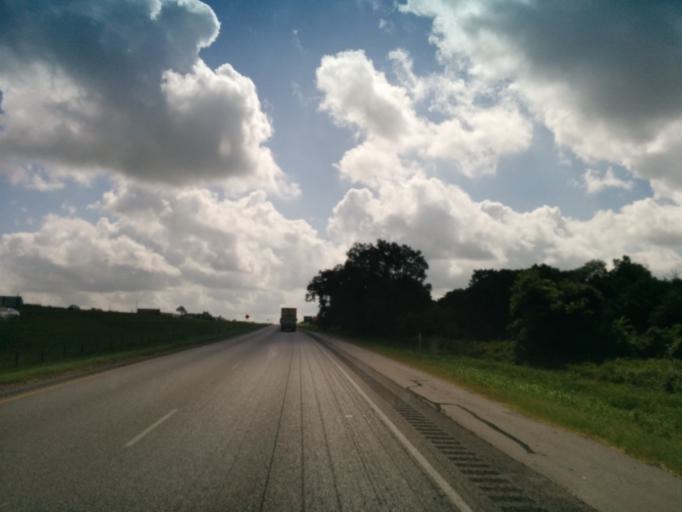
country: US
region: Texas
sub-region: Fayette County
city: Schulenburg
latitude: 29.6908
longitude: -96.9187
